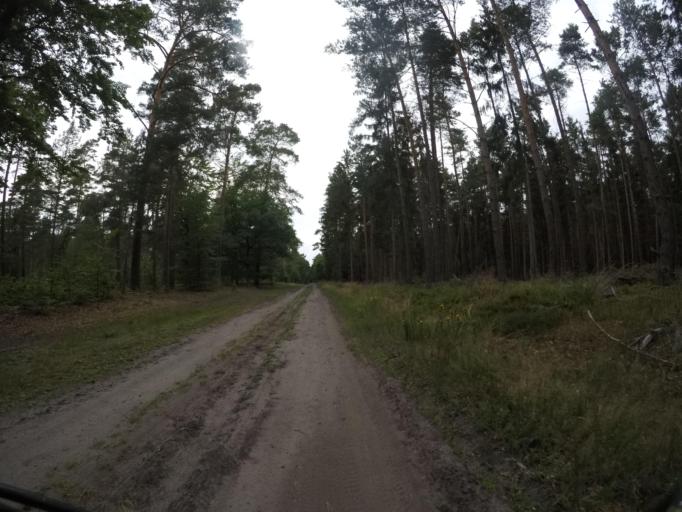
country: DE
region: Mecklenburg-Vorpommern
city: Lubtheen
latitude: 53.2587
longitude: 11.0025
